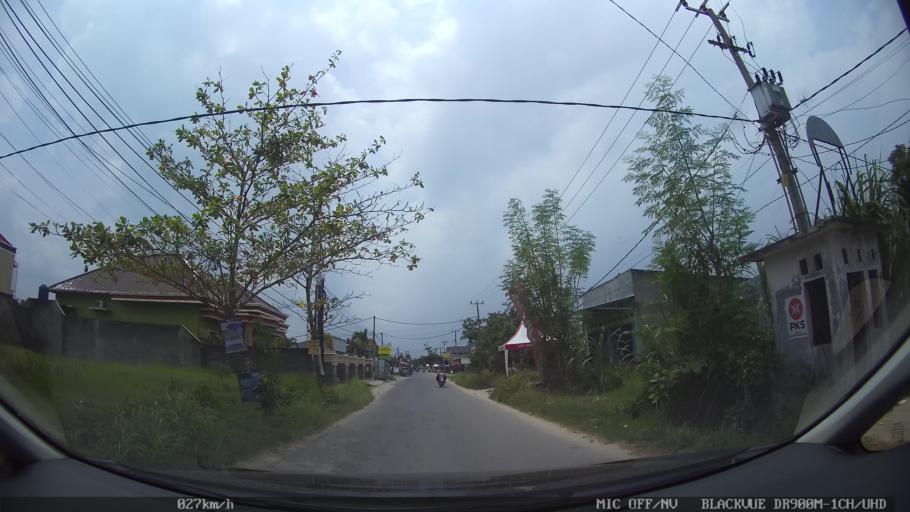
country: ID
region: Lampung
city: Kedaton
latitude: -5.3944
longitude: 105.3064
